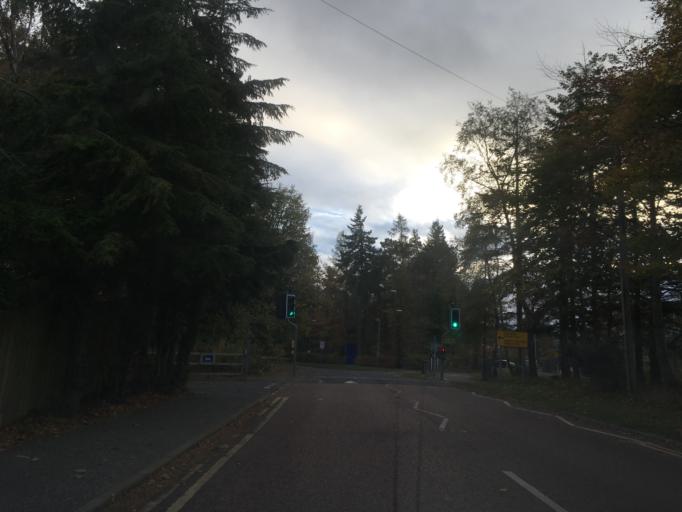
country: GB
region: Scotland
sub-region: Midlothian
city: Penicuik
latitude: 55.8649
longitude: -3.2009
